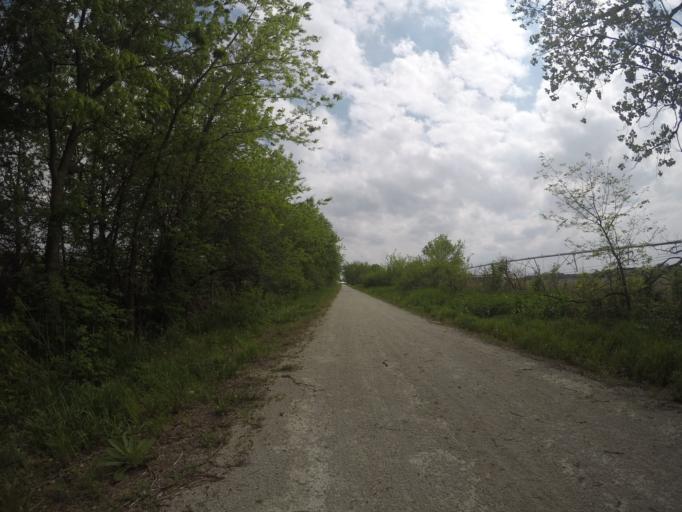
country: US
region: Kansas
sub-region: Marshall County
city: Marysville
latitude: 39.9472
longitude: -96.6104
